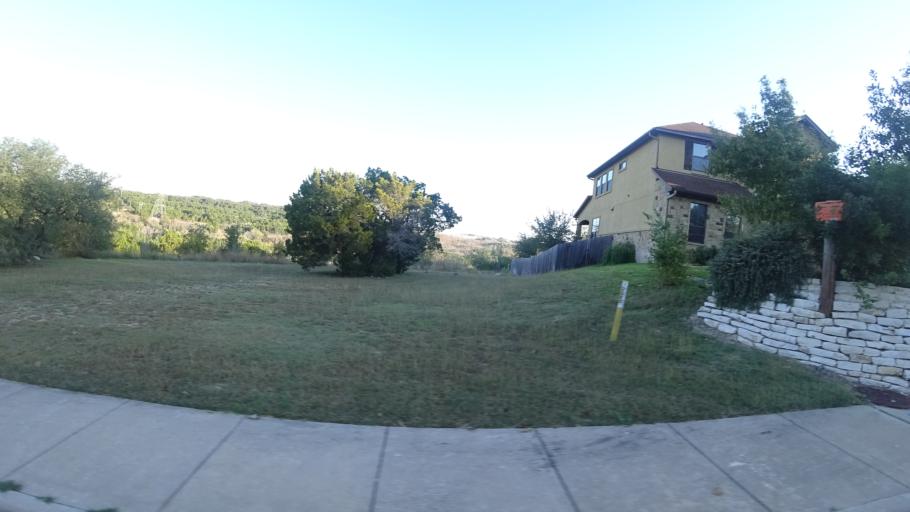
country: US
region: Texas
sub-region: Travis County
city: Hudson Bend
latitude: 30.3818
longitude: -97.8958
